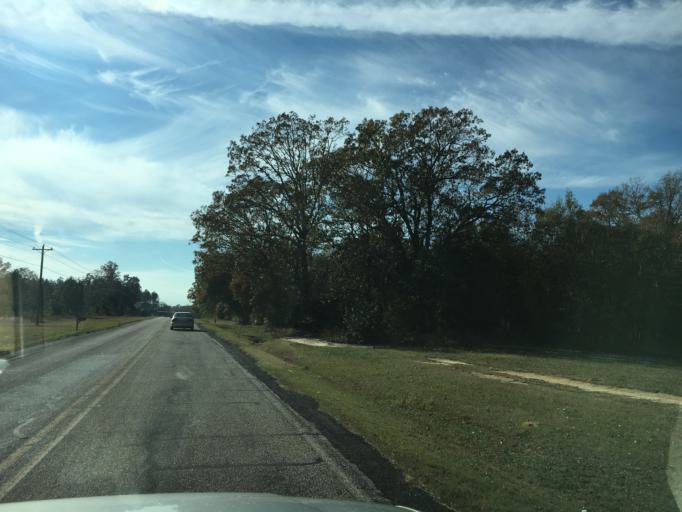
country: US
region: Georgia
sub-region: Hart County
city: Hartwell
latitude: 34.2865
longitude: -82.8603
